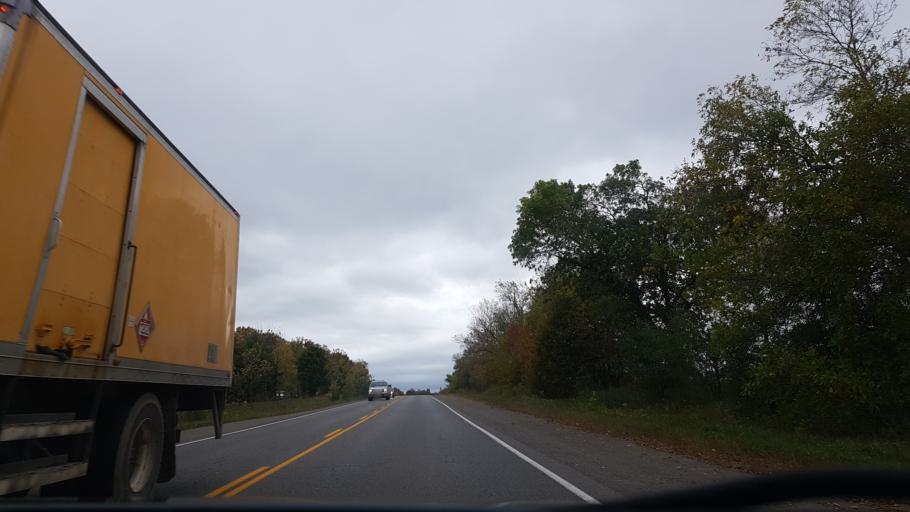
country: CA
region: Ontario
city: Peterborough
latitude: 44.2560
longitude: -78.3993
